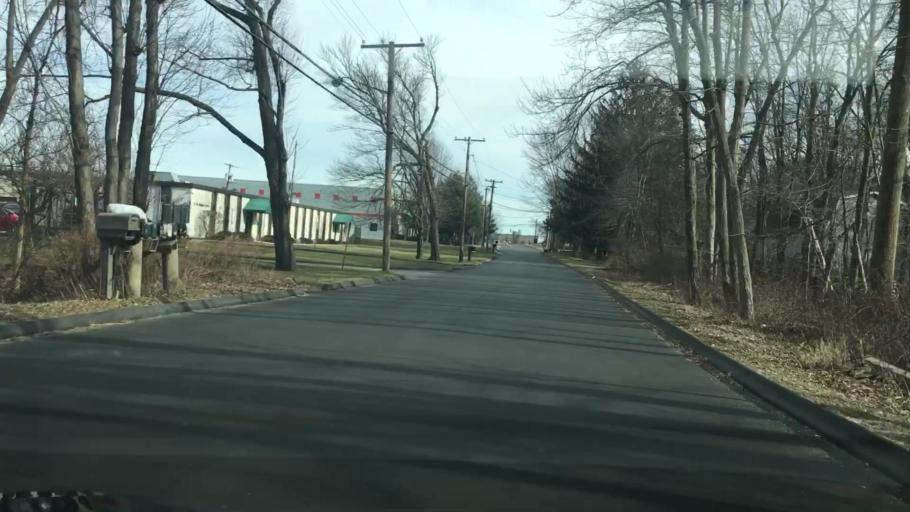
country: US
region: New York
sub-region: Putnam County
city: Peach Lake
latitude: 41.3805
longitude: -73.5191
